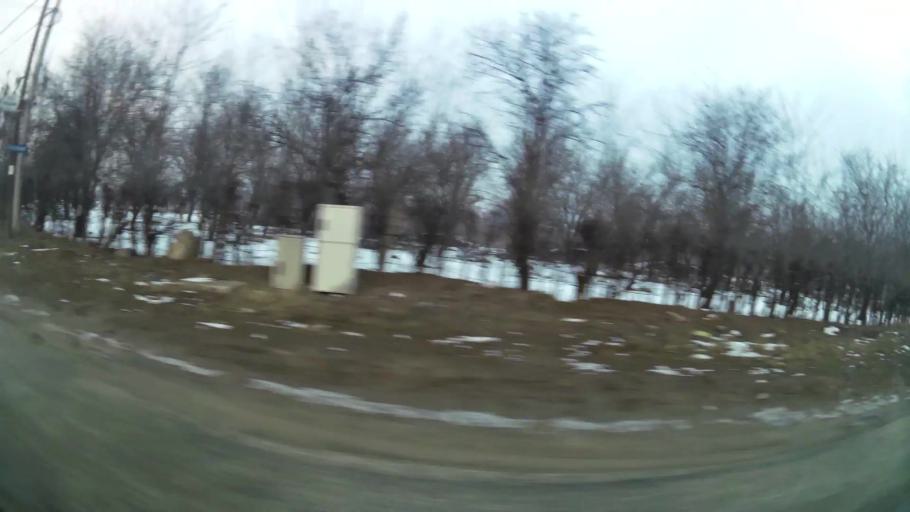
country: MK
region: Suto Orizari
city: Suto Orizare
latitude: 42.0298
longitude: 21.4071
